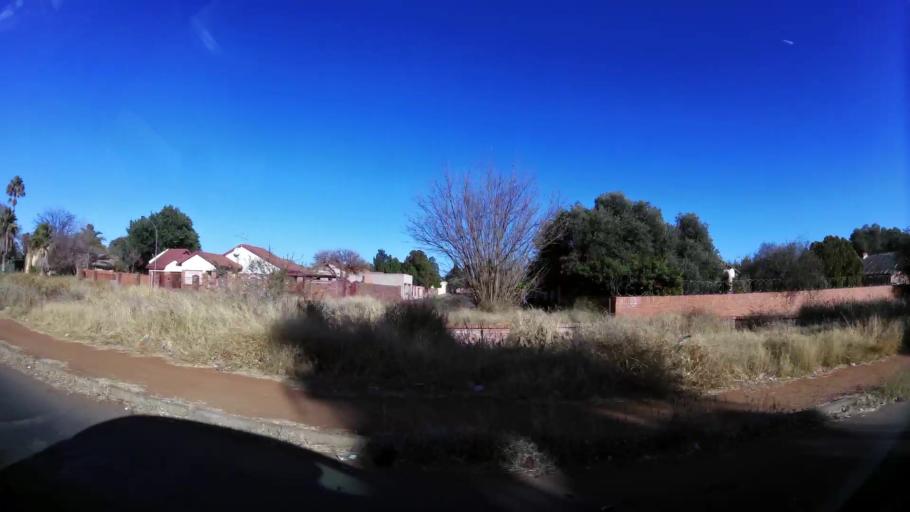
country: ZA
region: Northern Cape
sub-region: Frances Baard District Municipality
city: Kimberley
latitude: -28.7378
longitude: 24.7305
